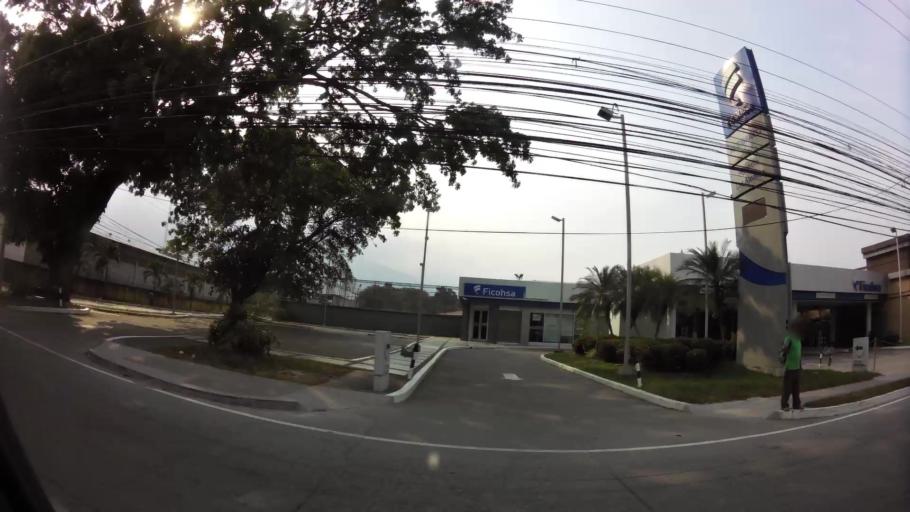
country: HN
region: Cortes
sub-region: San Pedro Sula
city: Pena Blanca
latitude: 15.5465
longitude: -88.0120
